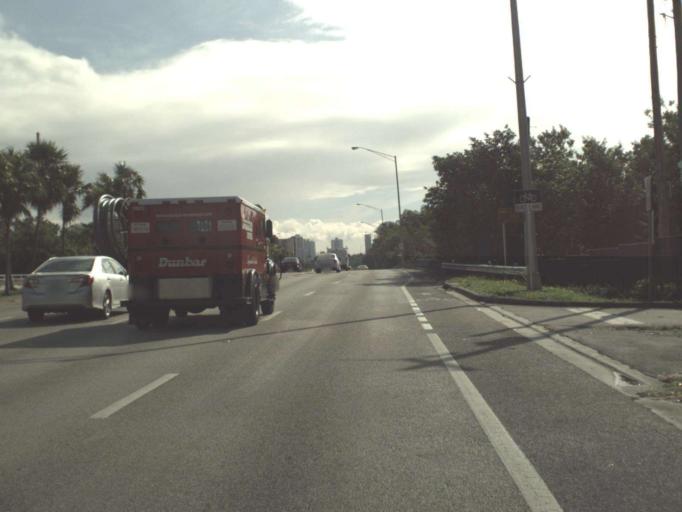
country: US
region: Florida
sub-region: Miami-Dade County
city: North Miami Beach
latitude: 25.9258
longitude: -80.1503
